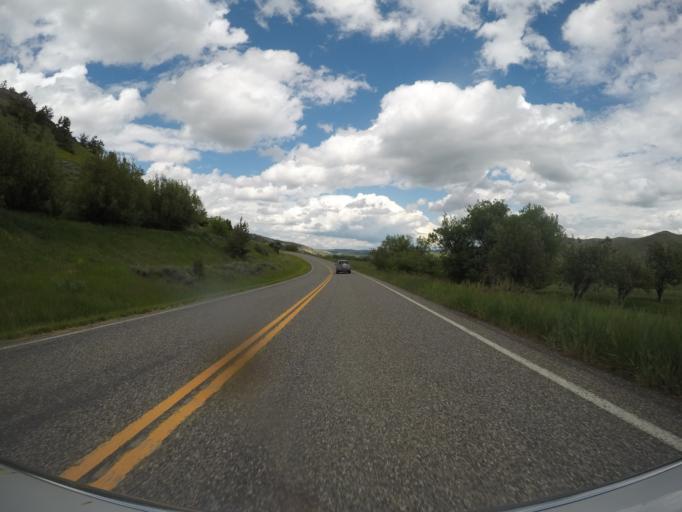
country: US
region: Montana
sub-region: Sweet Grass County
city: Big Timber
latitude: 45.6857
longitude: -110.0786
